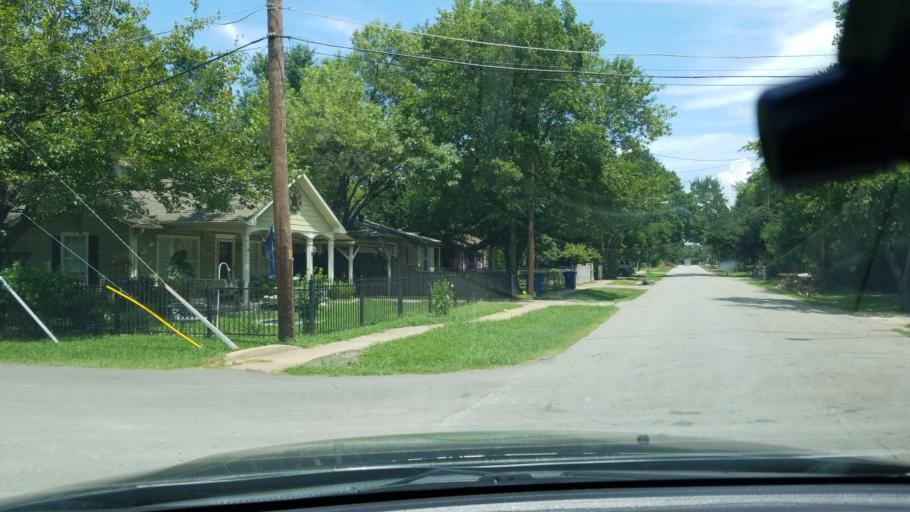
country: US
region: Texas
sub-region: Dallas County
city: Balch Springs
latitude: 32.7452
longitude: -96.6399
